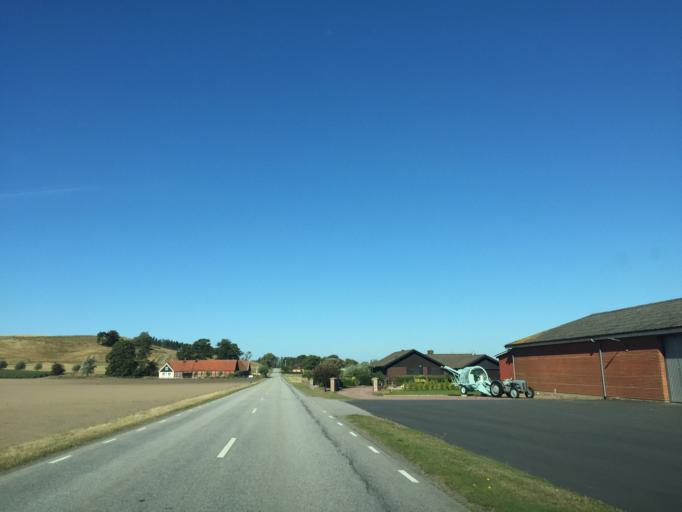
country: SE
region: Skane
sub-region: Ystads Kommun
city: Kopingebro
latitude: 55.3905
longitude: 14.0880
